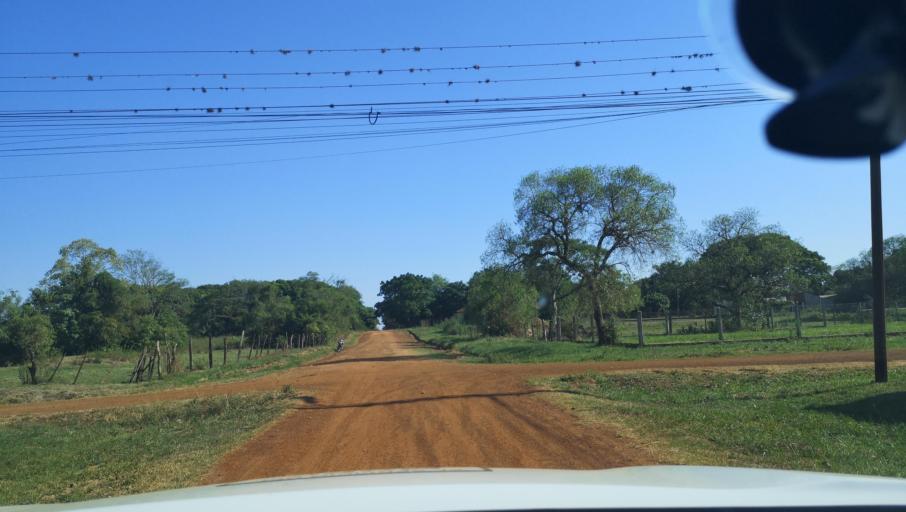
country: PY
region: Itapua
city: Carmen del Parana
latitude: -27.1699
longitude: -56.2370
